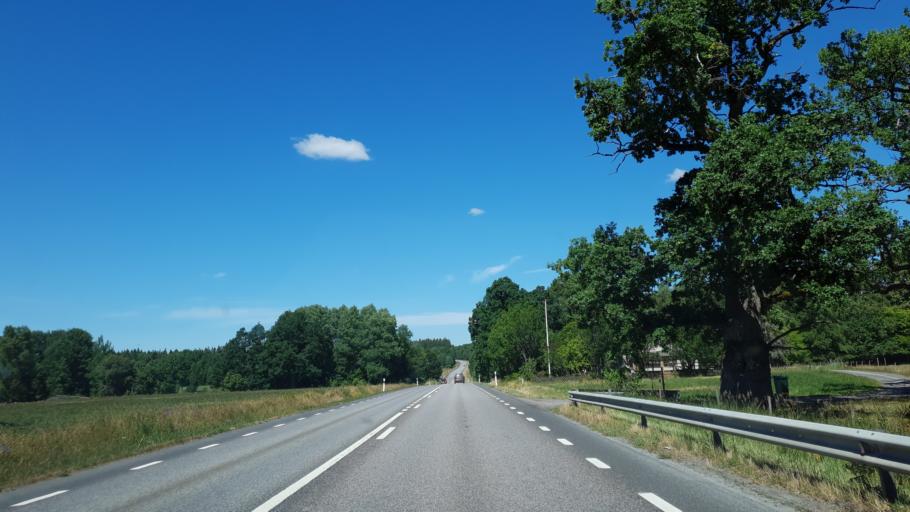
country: SE
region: Joenkoeping
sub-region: Varnamo Kommun
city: Bor
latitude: 57.1319
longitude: 14.1230
